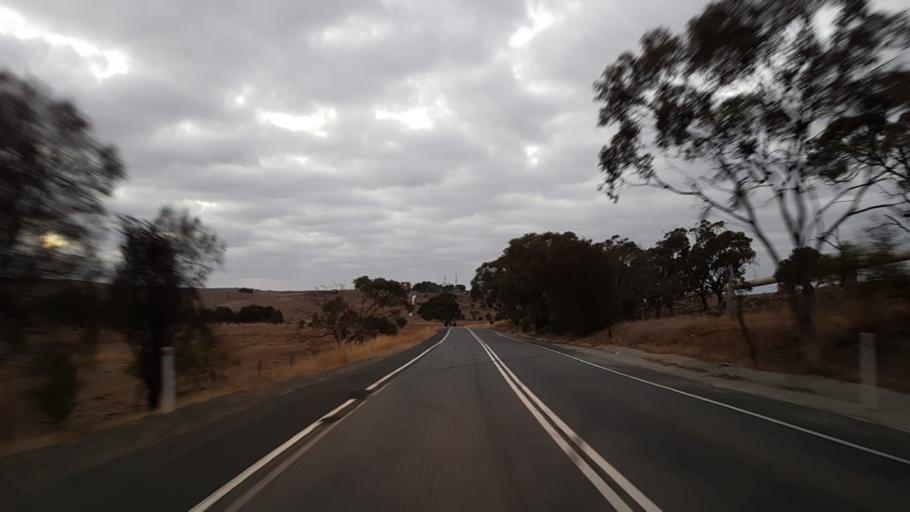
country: AU
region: South Australia
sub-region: Mount Barker
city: Callington
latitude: -35.0521
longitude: 139.0053
